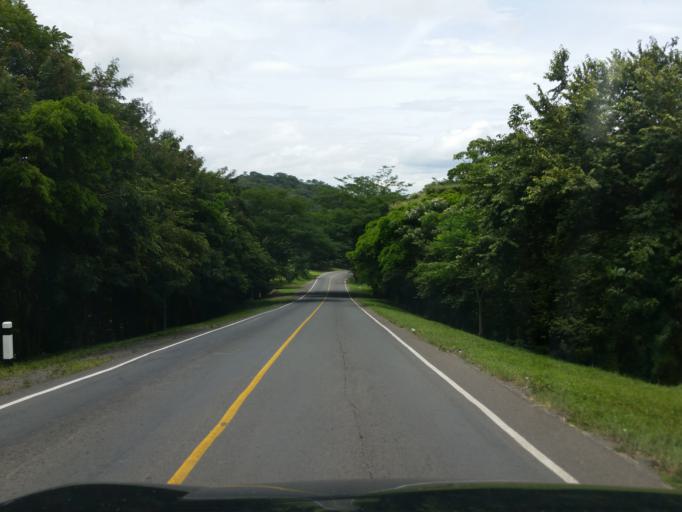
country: NI
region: Matagalpa
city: Matagalpa
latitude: 12.9404
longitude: -85.8797
